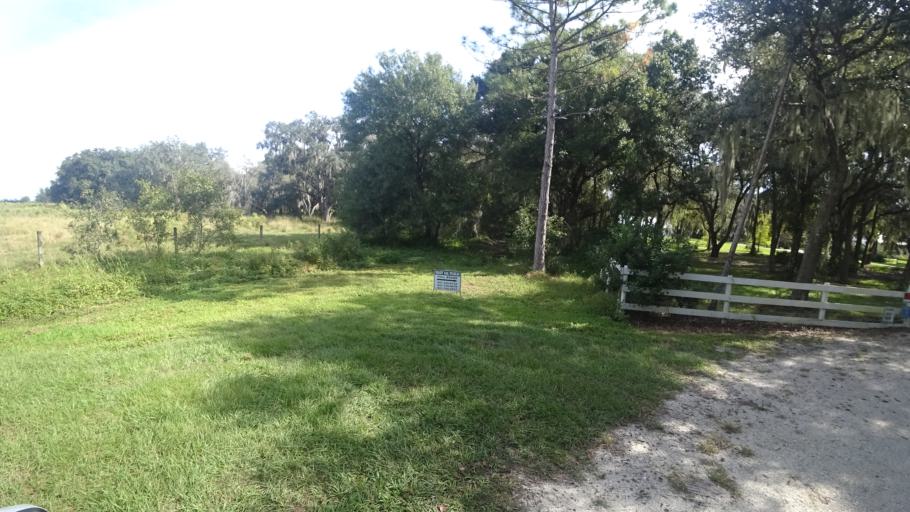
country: US
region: Florida
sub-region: Sarasota County
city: The Meadows
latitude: 27.4162
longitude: -82.2960
